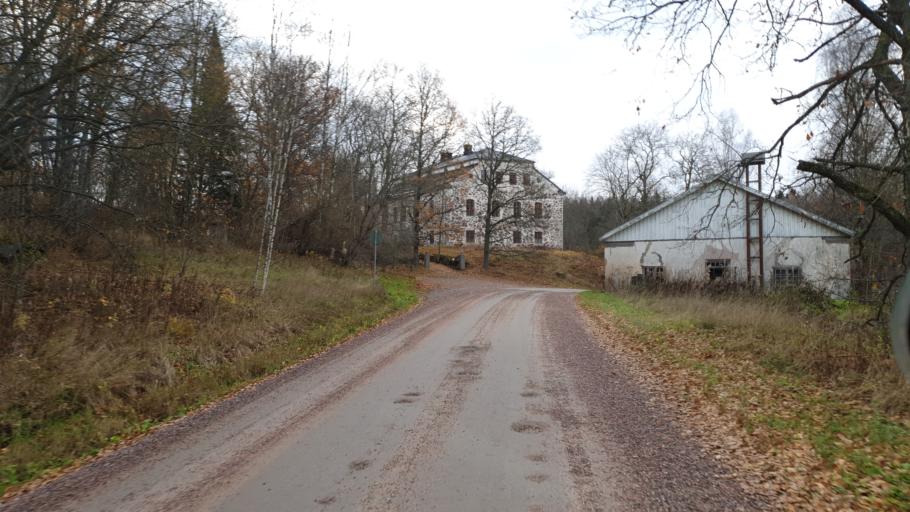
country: FI
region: Uusimaa
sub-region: Helsinki
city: Siuntio
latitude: 60.1419
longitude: 24.2631
